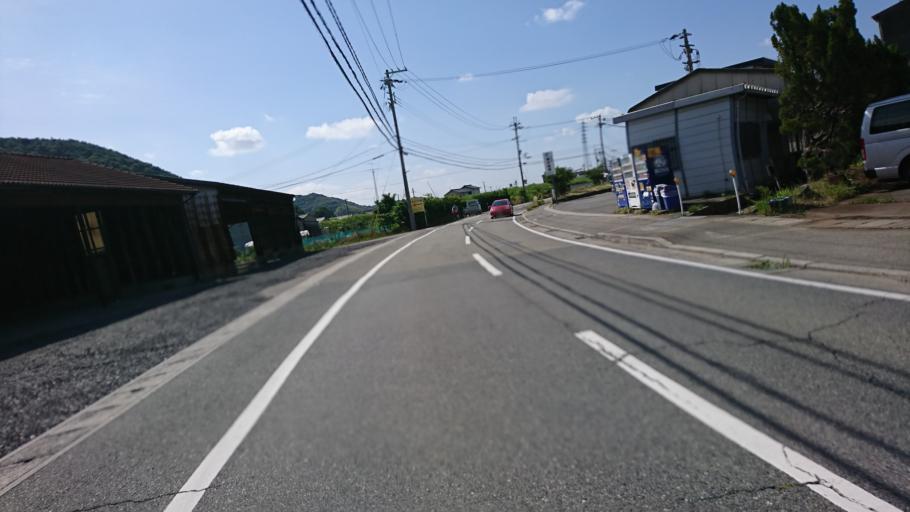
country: JP
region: Hyogo
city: Shirahamacho-usazakiminami
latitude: 34.7930
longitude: 134.7489
